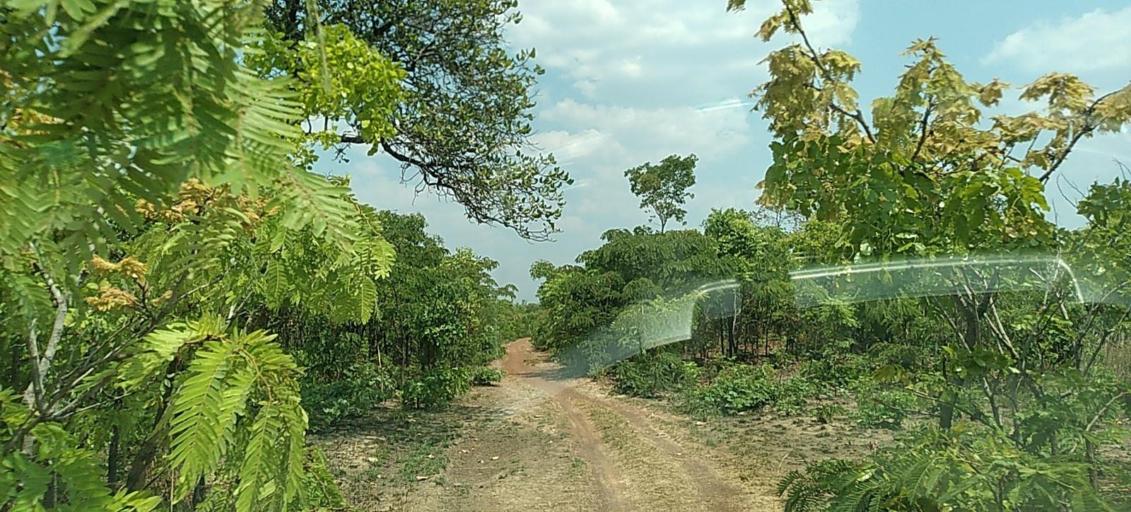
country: CD
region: Katanga
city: Kipushi
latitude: -12.0121
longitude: 27.4323
